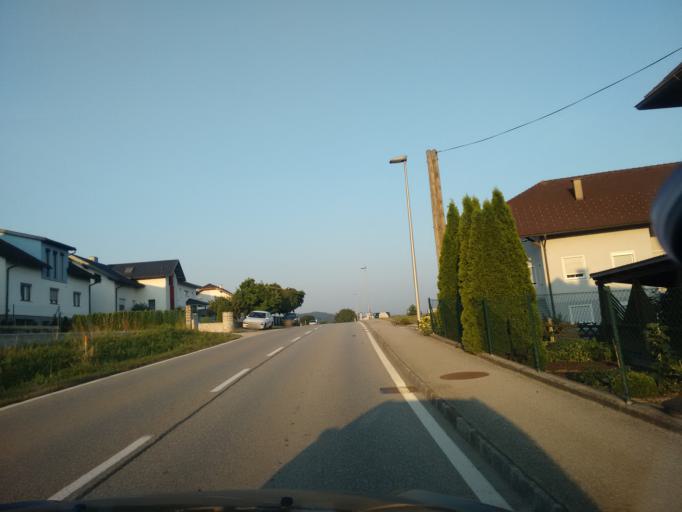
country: AT
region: Upper Austria
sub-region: Politischer Bezirk Grieskirchen
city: Bad Schallerbach
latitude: 48.1864
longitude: 13.9113
